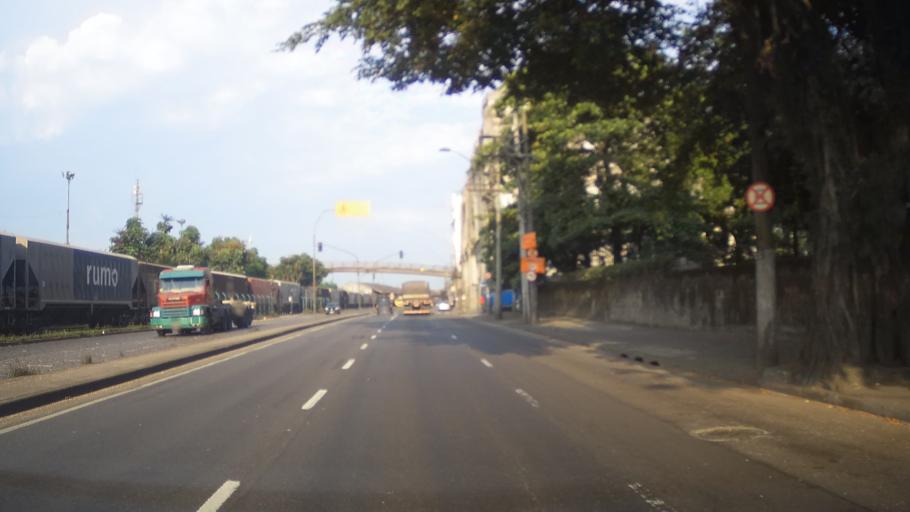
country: BR
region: Sao Paulo
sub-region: Santos
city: Santos
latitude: -23.9323
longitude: -46.3259
